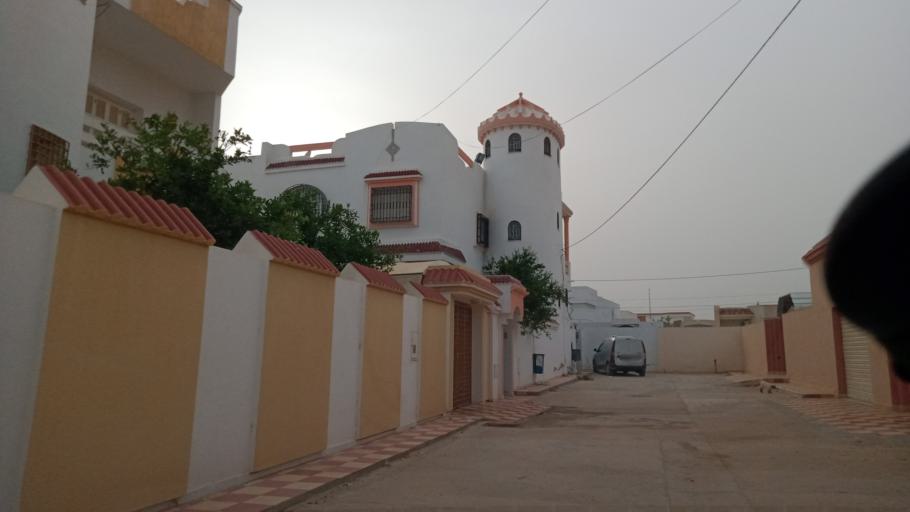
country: TN
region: Safaqis
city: Al Qarmadah
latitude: 34.7972
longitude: 10.7671
